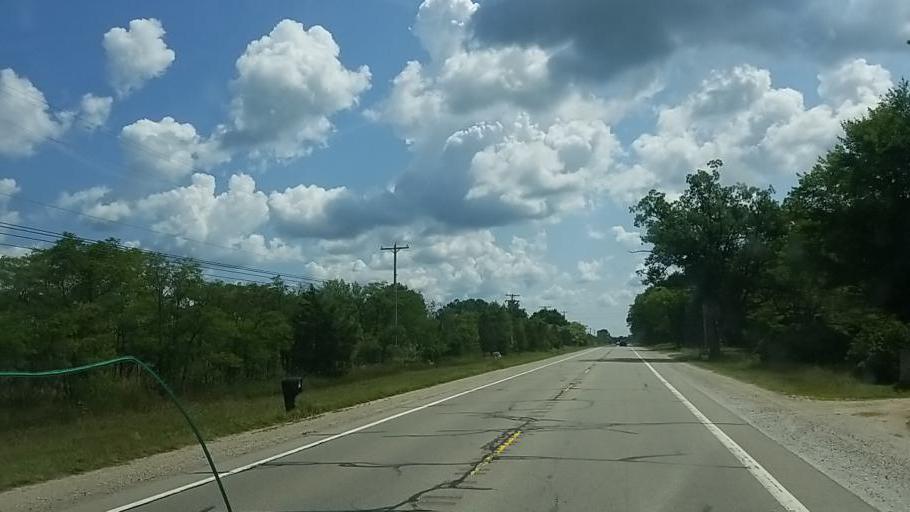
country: US
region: Michigan
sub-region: Muskegon County
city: Wolf Lake
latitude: 43.2353
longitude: -86.0413
